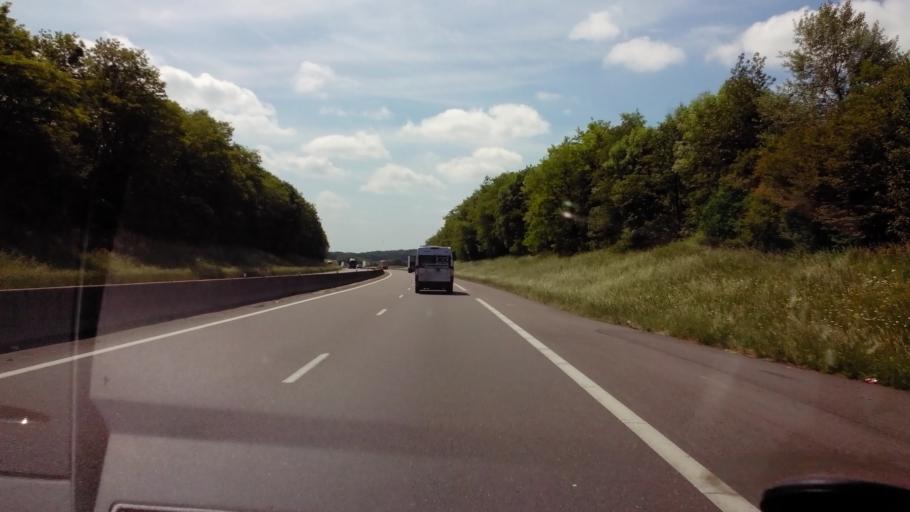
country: FR
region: Lorraine
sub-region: Departement des Vosges
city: Chatenois
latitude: 48.3909
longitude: 5.8796
